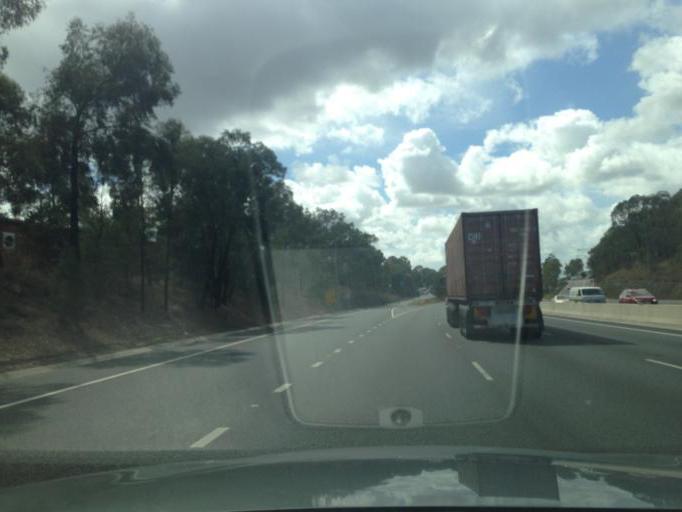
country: AU
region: New South Wales
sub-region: Bankstown
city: Padstow
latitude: -33.9398
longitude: 151.0307
